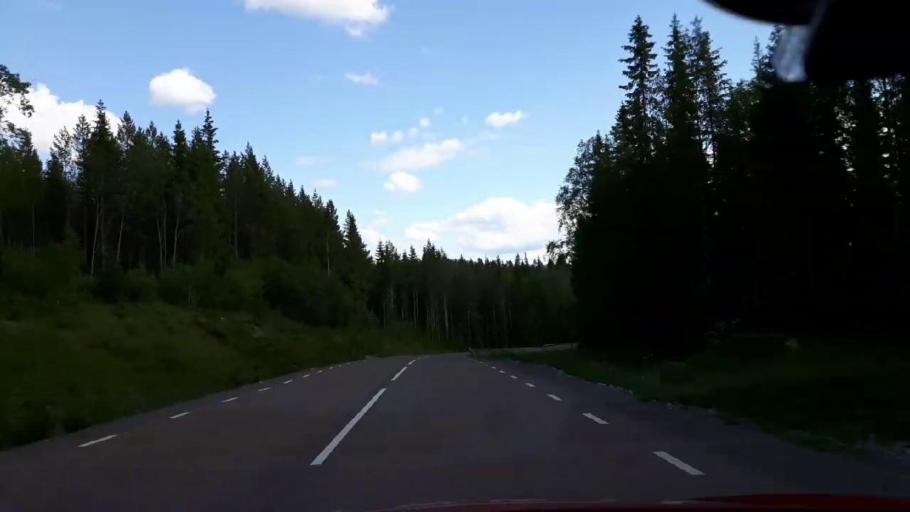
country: SE
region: Jaemtland
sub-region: Krokoms Kommun
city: Valla
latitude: 64.0539
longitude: 14.1681
